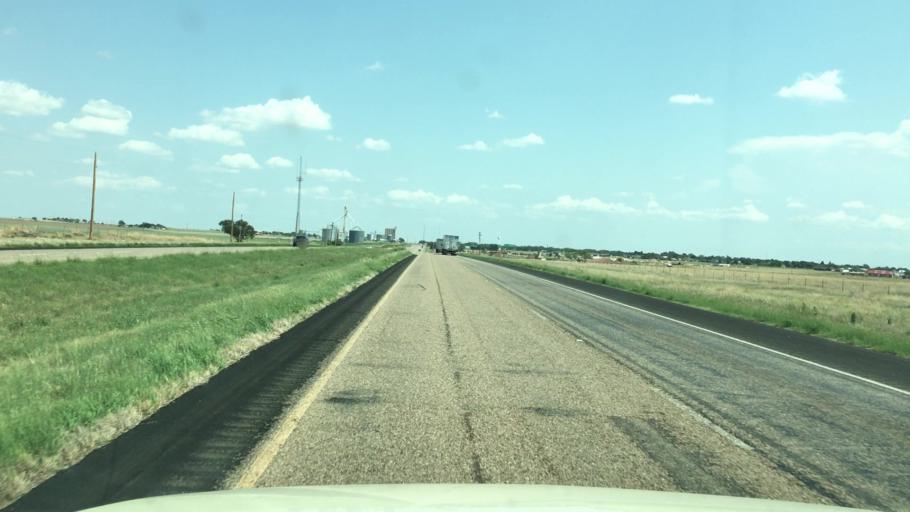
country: US
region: Texas
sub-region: Armstrong County
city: Claude
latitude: 35.1215
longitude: -101.3870
